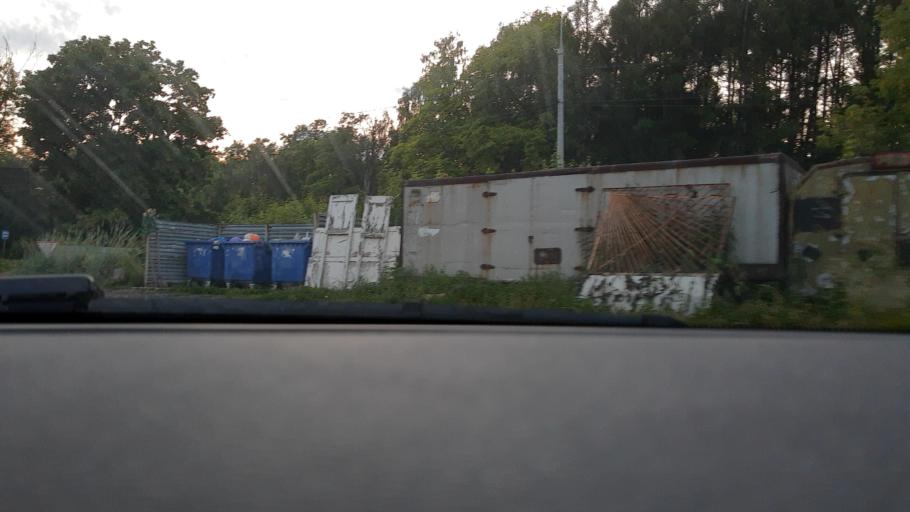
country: RU
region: Nizjnij Novgorod
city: Kstovo
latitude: 56.1568
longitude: 44.2554
